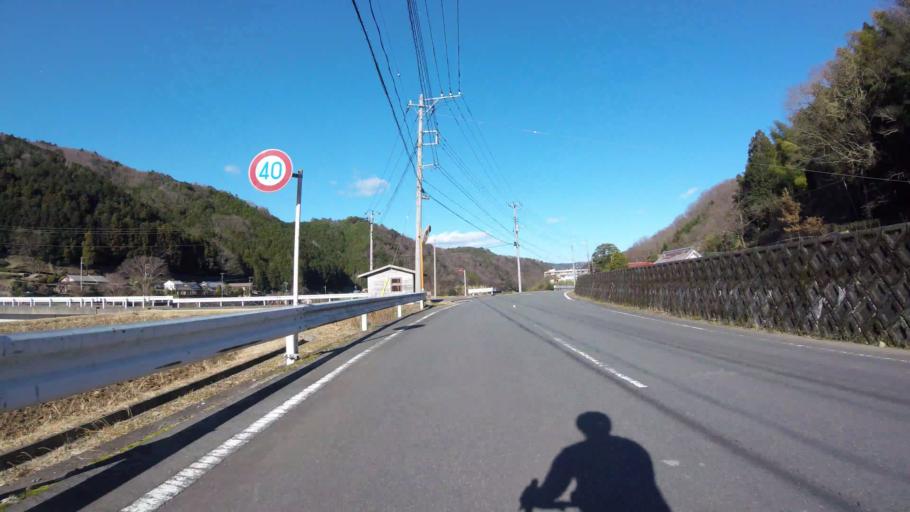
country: JP
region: Shizuoka
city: Ito
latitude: 34.9292
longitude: 138.9909
